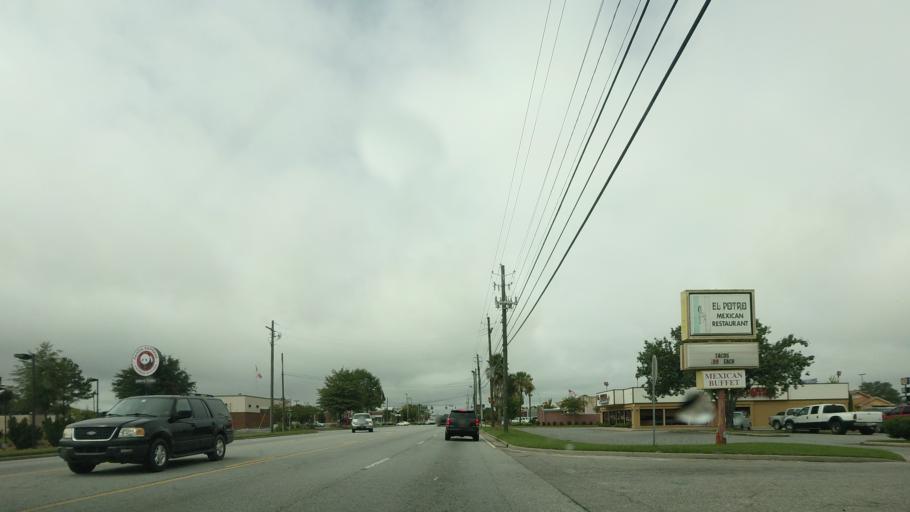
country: US
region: Georgia
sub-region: Lowndes County
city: Remerton
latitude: 30.8394
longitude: -83.3192
